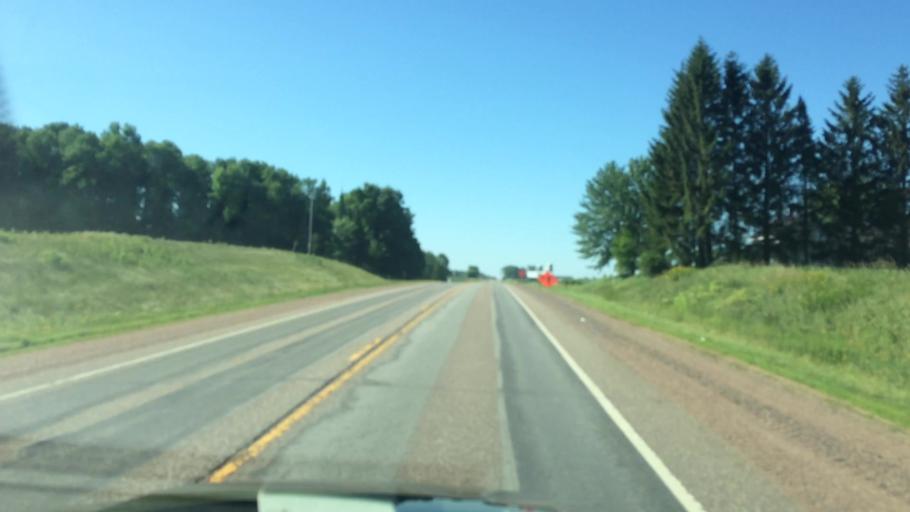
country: US
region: Wisconsin
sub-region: Marathon County
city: Stratford
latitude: 44.9106
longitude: -90.0786
